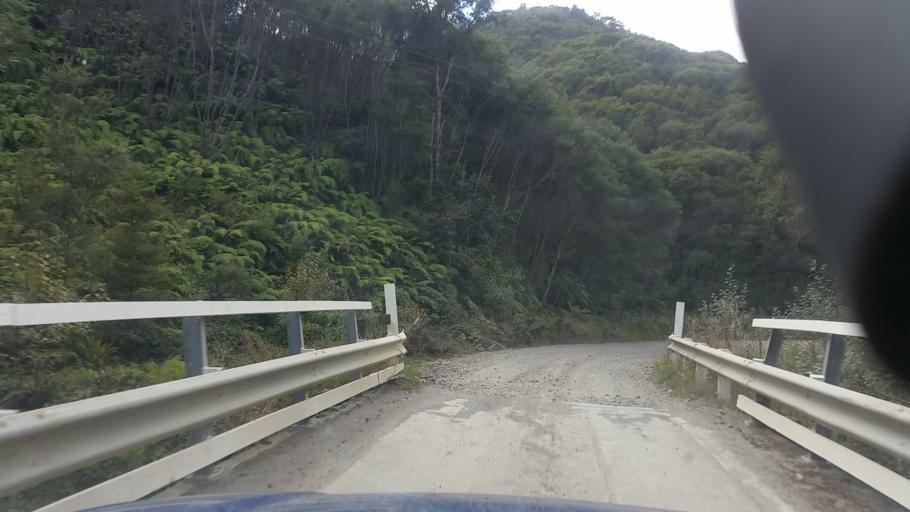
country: NZ
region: Taranaki
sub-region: New Plymouth District
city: Waitara
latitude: -39.0249
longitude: 174.8234
